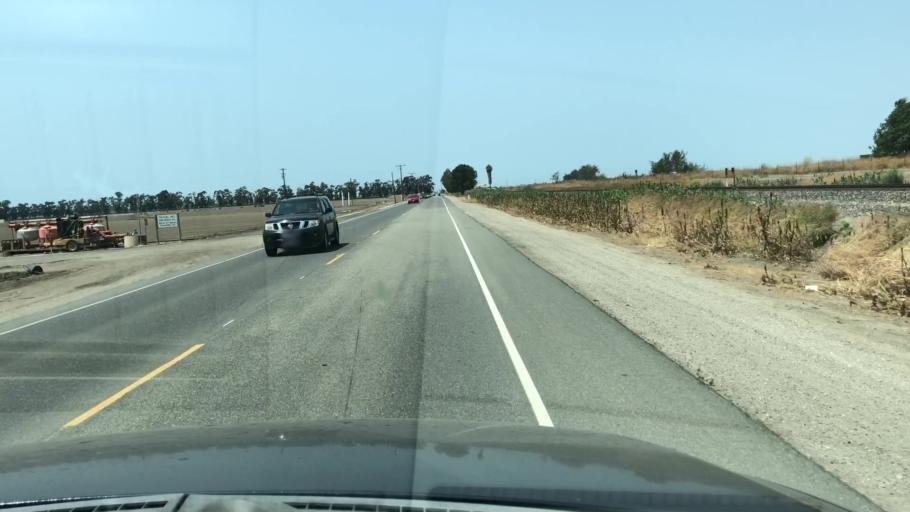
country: US
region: California
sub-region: Ventura County
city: Camarillo
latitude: 34.1961
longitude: -119.0755
